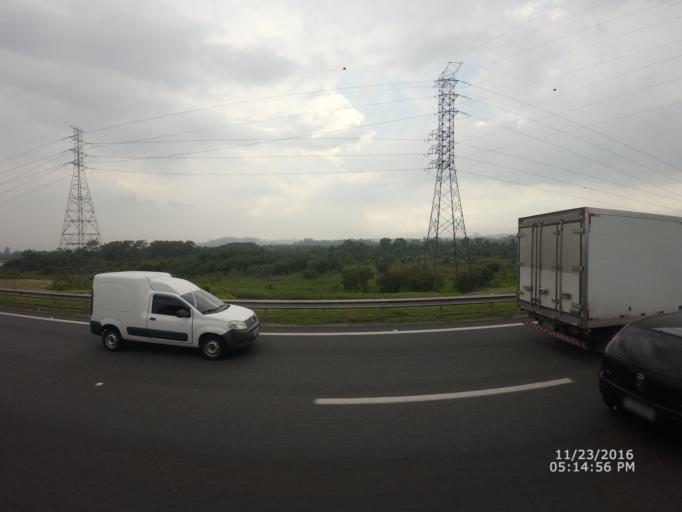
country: BR
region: Sao Paulo
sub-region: Guarulhos
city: Guarulhos
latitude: -23.4774
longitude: -46.5170
